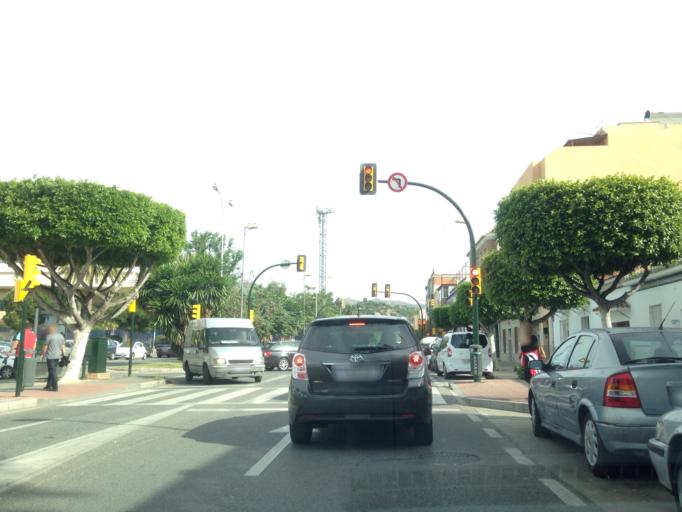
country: ES
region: Andalusia
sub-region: Provincia de Malaga
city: Malaga
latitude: 36.7499
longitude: -4.4222
